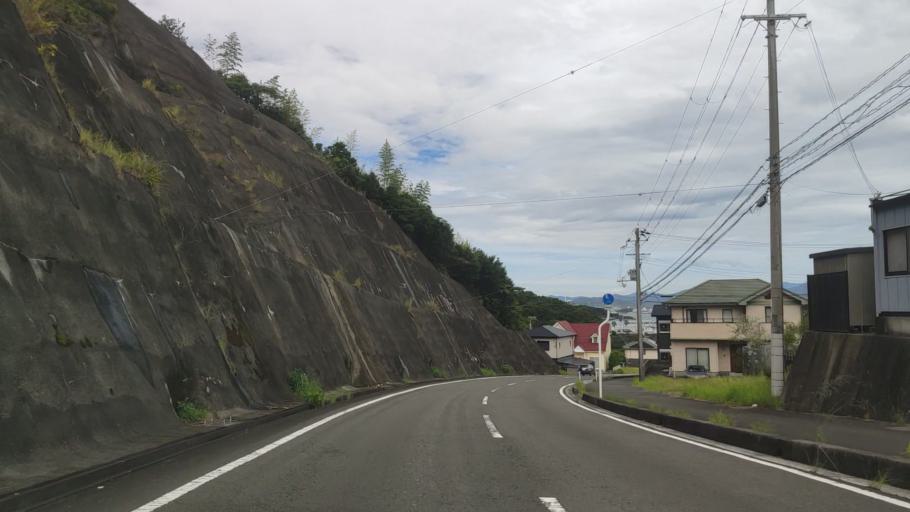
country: JP
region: Wakayama
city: Tanabe
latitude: 33.6883
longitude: 135.3884
